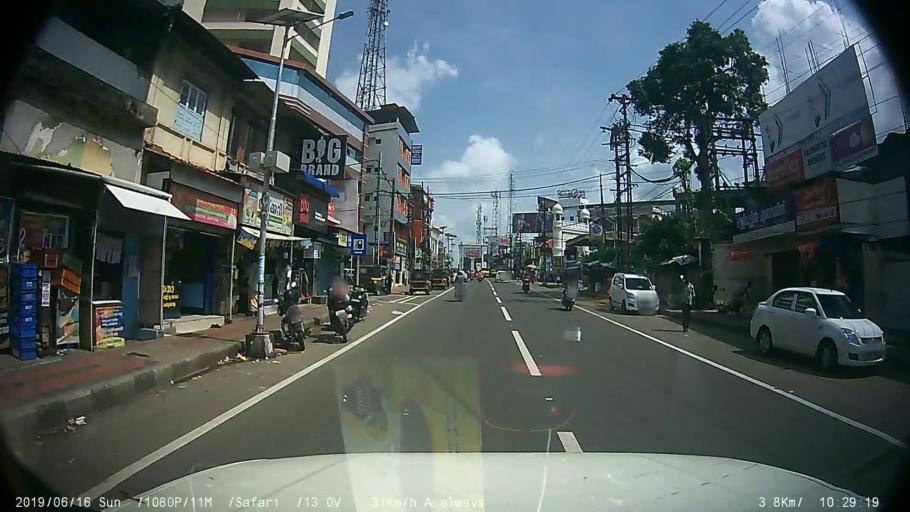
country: IN
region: Kerala
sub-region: Kottayam
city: Changanacheri
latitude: 9.4447
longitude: 76.5419
